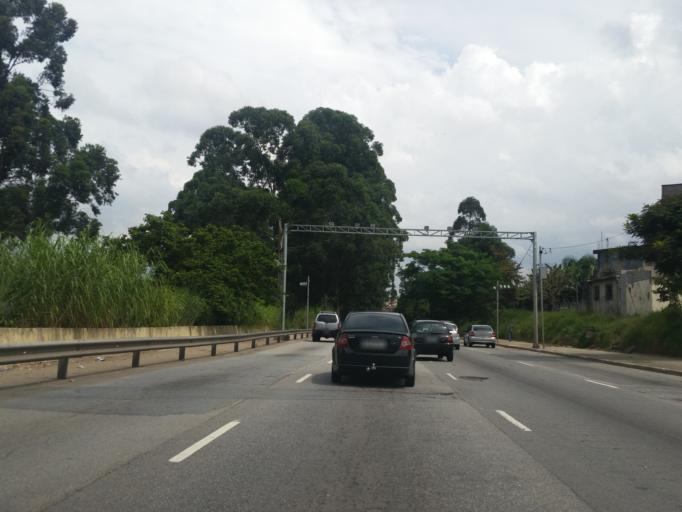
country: BR
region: Sao Paulo
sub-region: Ferraz De Vasconcelos
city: Ferraz de Vasconcelos
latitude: -23.5224
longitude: -46.4565
